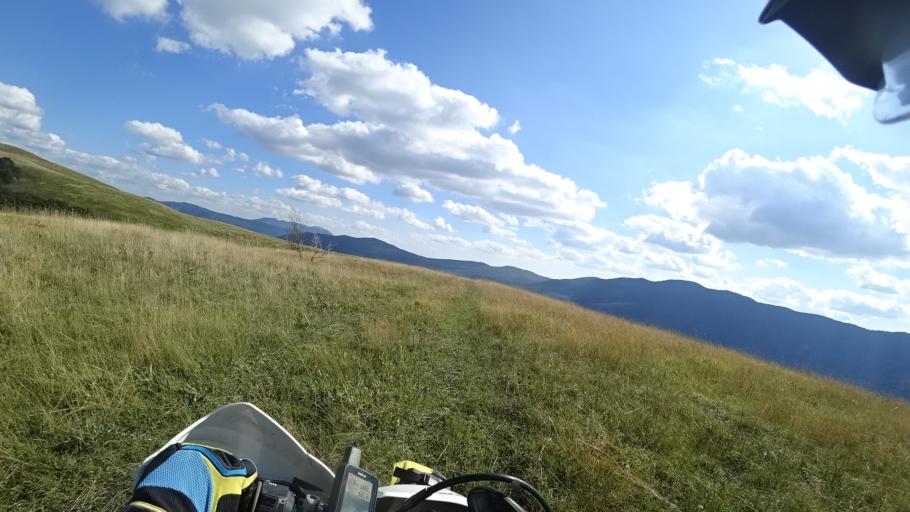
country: HR
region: Zadarska
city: Gracac
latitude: 44.3774
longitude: 16.0522
